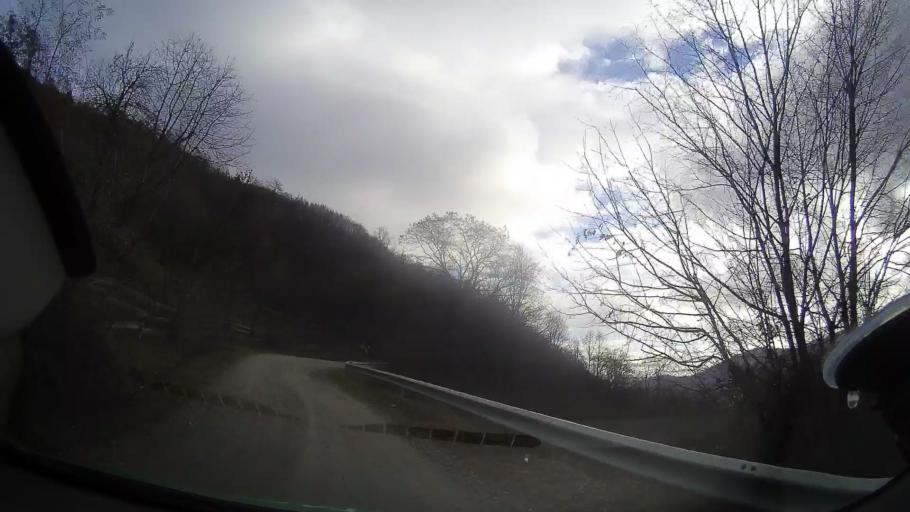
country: RO
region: Cluj
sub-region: Comuna Valea Ierii
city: Valea Ierii
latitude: 46.6469
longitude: 23.3482
